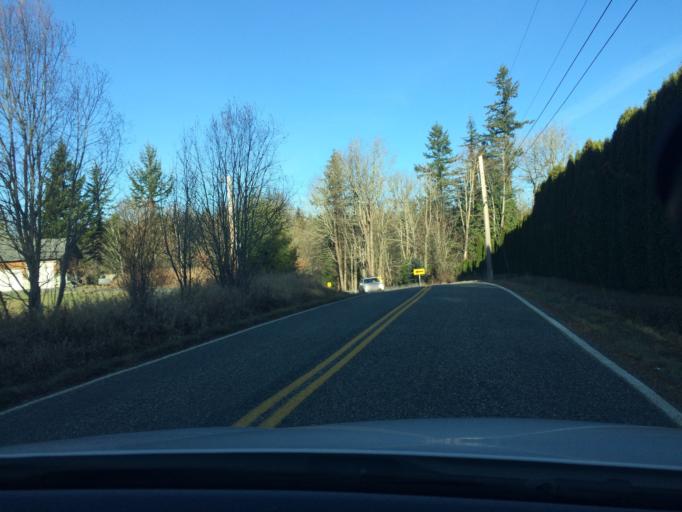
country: US
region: Washington
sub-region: Whatcom County
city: Everson
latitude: 48.8450
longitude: -122.3975
